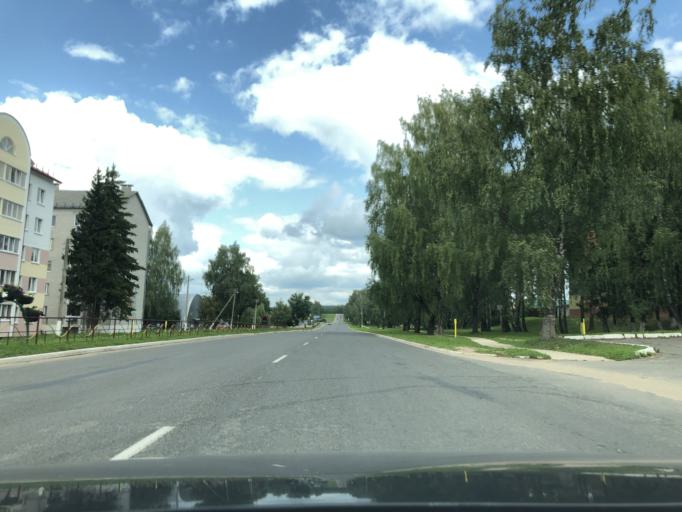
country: BY
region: Minsk
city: Lahoysk
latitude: 54.2176
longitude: 27.8513
